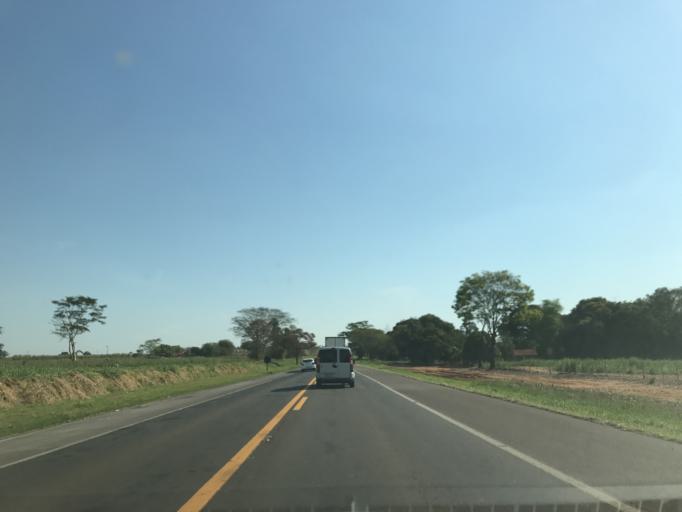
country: BR
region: Sao Paulo
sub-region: Penapolis
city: Penapolis
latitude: -21.4779
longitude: -50.1992
